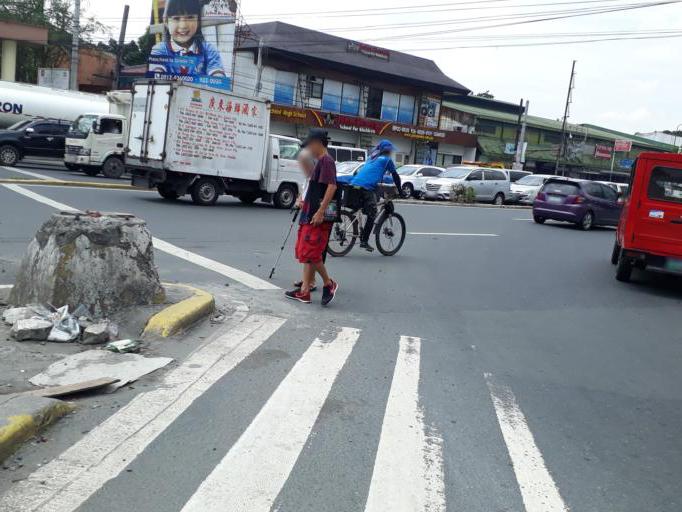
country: PH
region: Calabarzon
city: Bagong Pagasa
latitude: 14.6680
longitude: 121.0336
